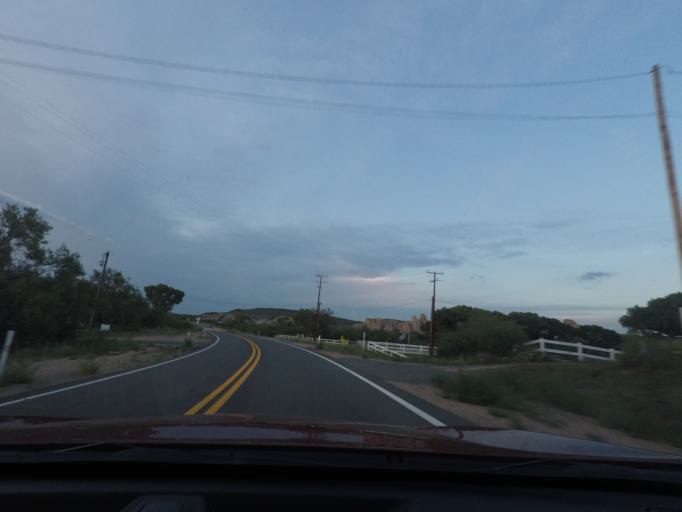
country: US
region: Arizona
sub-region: Yavapai County
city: Prescott
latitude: 34.4309
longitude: -112.6932
